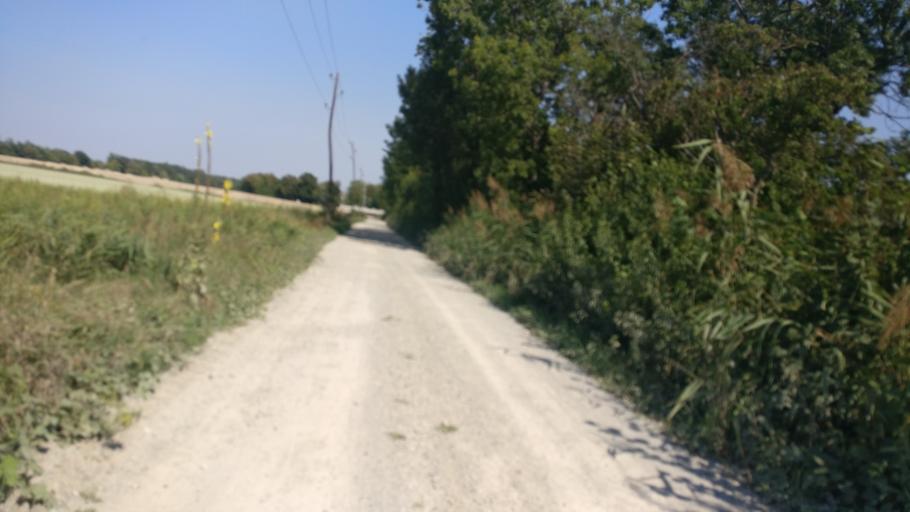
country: AT
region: Lower Austria
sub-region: Politischer Bezirk Baden
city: Ebreichsdorf
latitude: 47.9833
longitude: 16.4072
